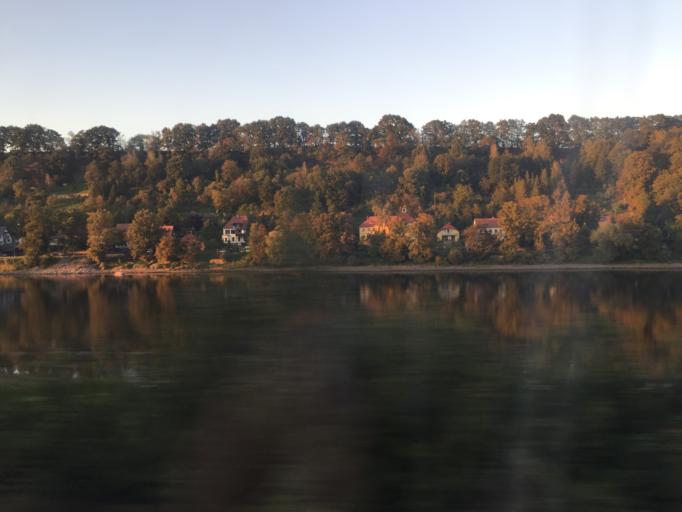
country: DE
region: Saxony
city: Pirna
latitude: 50.9621
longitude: 13.9606
